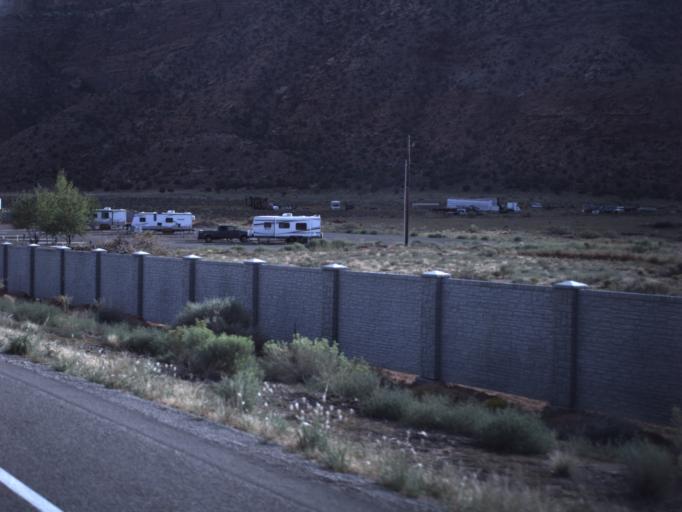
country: US
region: Utah
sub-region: Grand County
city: Moab
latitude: 38.4786
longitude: -109.4579
